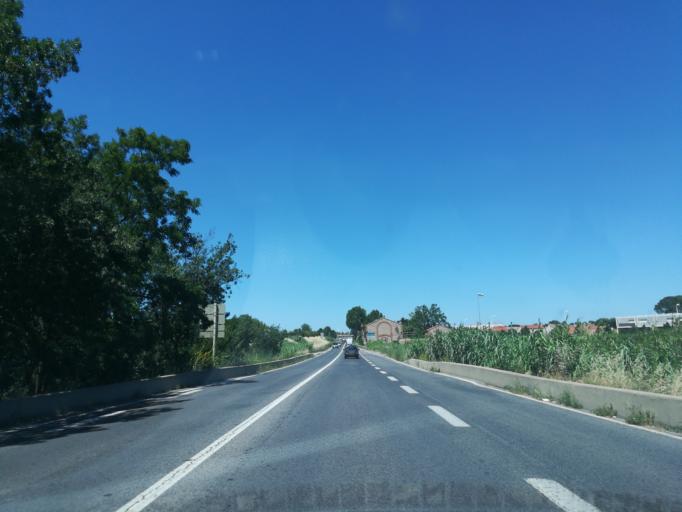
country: FR
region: Languedoc-Roussillon
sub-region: Departement des Pyrenees-Orientales
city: Pollestres
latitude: 42.6595
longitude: 2.8830
